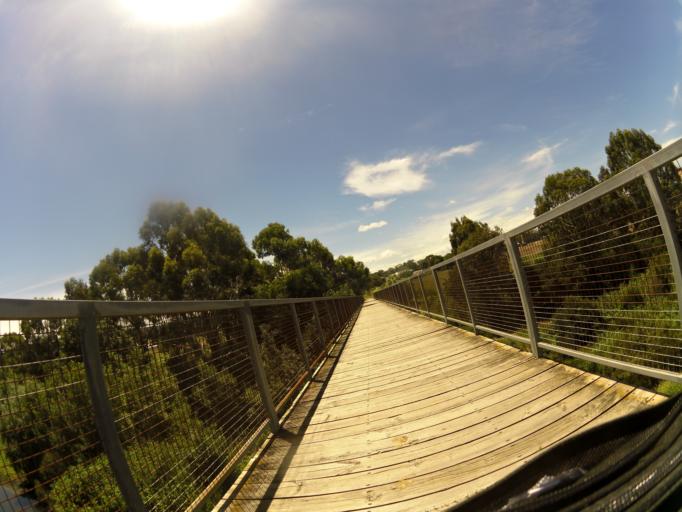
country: AU
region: Victoria
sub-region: East Gippsland
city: Lakes Entrance
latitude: -37.7107
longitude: 147.8328
